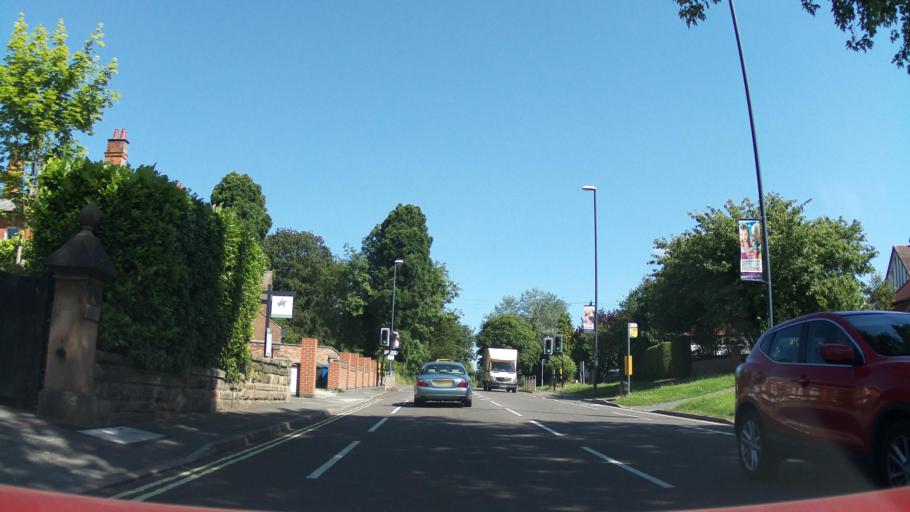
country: GB
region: England
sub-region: Derby
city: Derby
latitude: 52.9398
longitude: -1.4842
